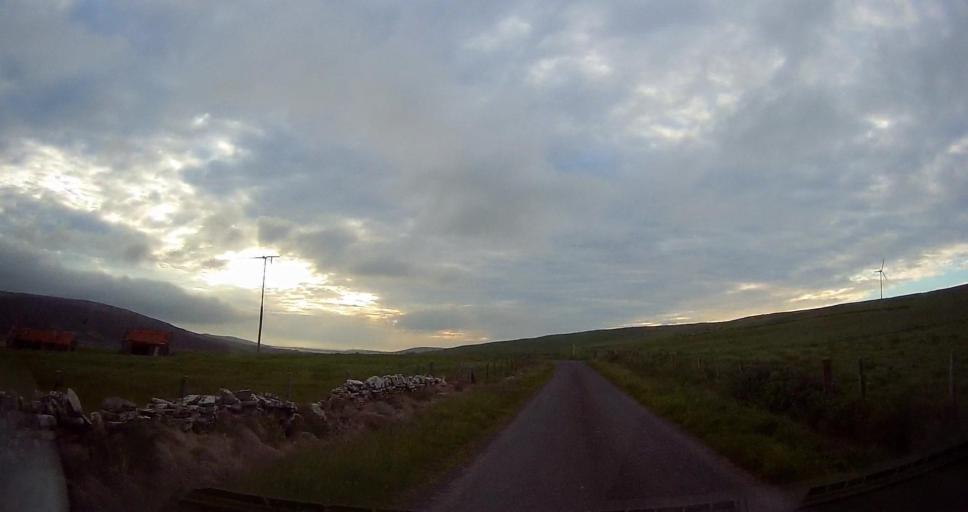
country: GB
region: Scotland
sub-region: Orkney Islands
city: Stromness
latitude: 59.0955
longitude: -3.1901
